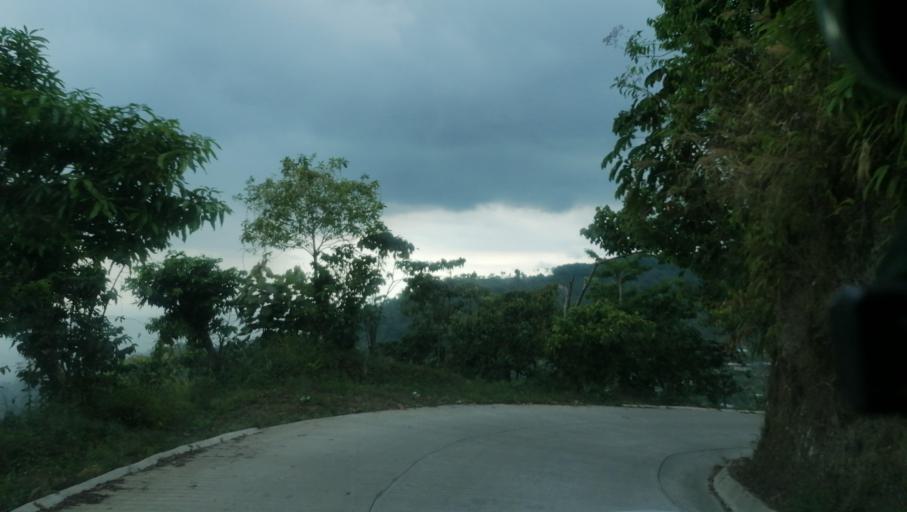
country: MX
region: Chiapas
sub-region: Cacahoatan
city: Benito Juarez
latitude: 15.0717
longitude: -92.1659
